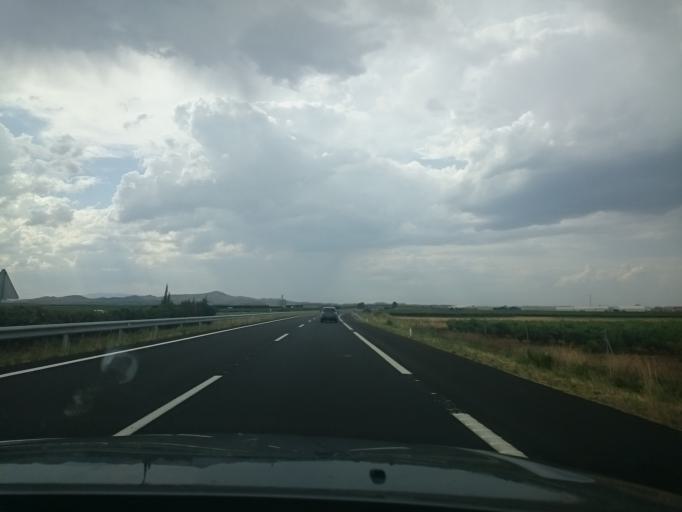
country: ES
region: La Rioja
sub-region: Provincia de La Rioja
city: Aldeanueva de Ebro
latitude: 42.2141
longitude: -1.8845
